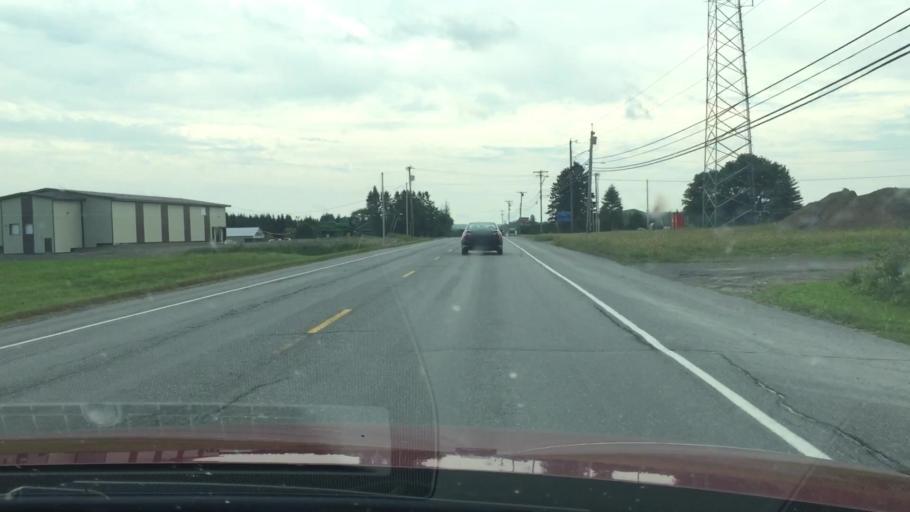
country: US
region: Maine
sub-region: Aroostook County
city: Houlton
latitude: 46.1637
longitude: -67.8407
